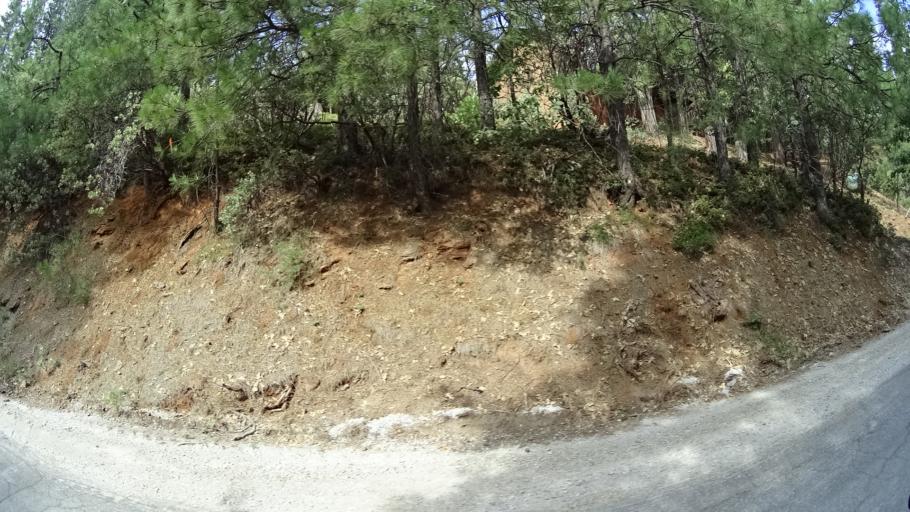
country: US
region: California
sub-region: Calaveras County
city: Arnold
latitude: 38.2467
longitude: -120.3413
